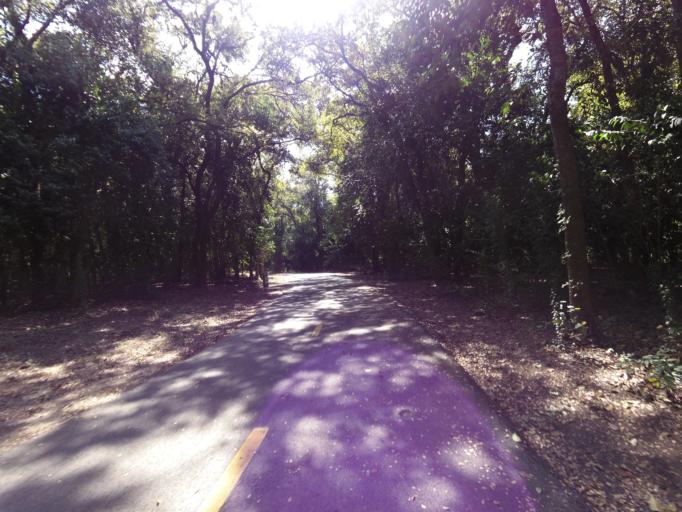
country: US
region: Texas
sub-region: Bexar County
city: Terrell Hills
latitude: 29.4204
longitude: -98.4291
